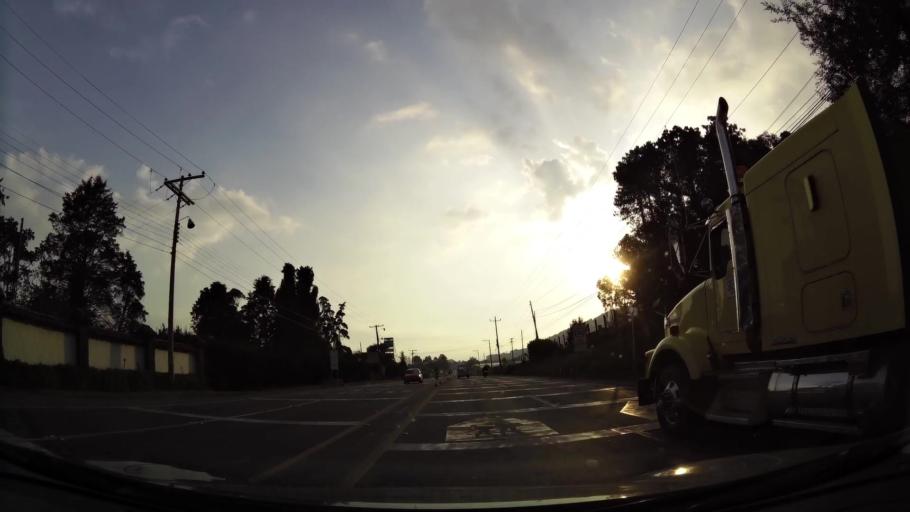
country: CO
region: Cundinamarca
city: Cota
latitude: 4.7835
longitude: -74.1289
